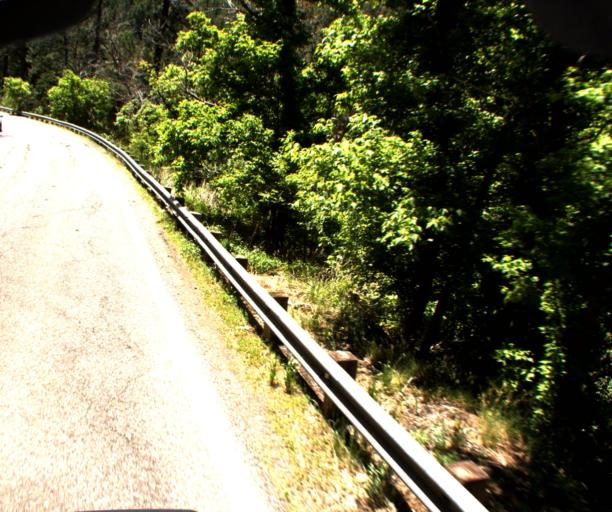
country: US
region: Arizona
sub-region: Coconino County
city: Sedona
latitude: 34.9715
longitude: -111.7497
